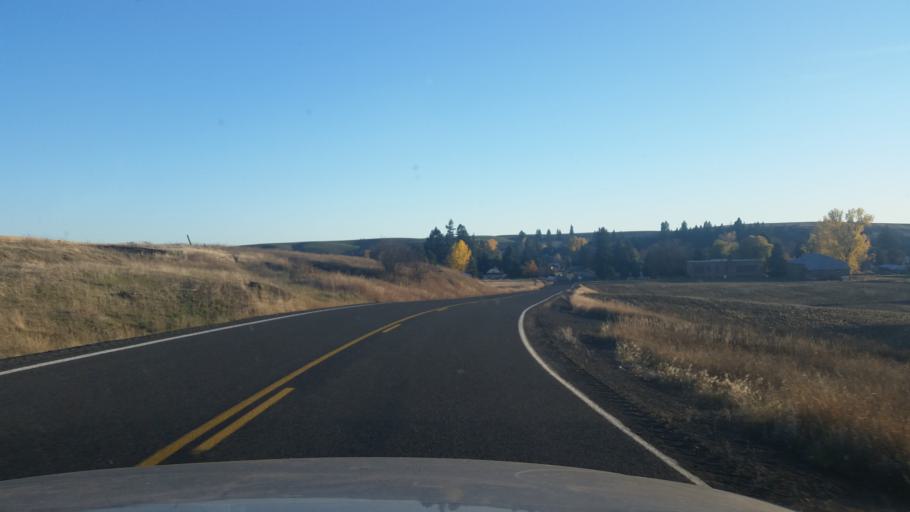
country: US
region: Washington
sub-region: Spokane County
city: Opportunity
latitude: 47.3479
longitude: -117.2279
